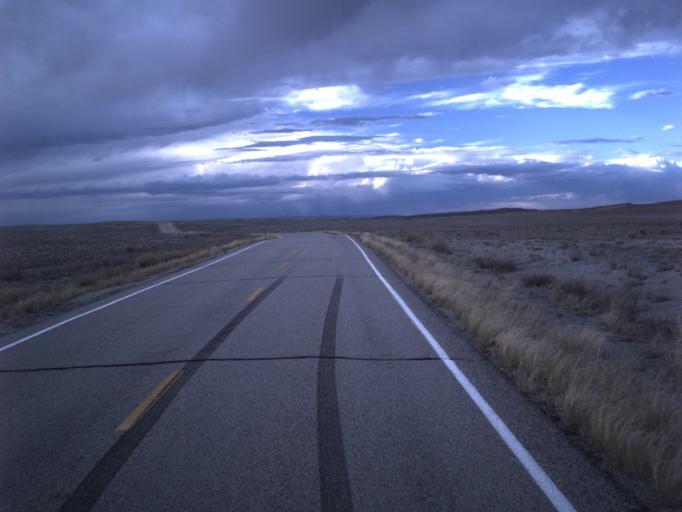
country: US
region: Utah
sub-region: Grand County
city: Moab
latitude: 38.8879
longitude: -109.3115
